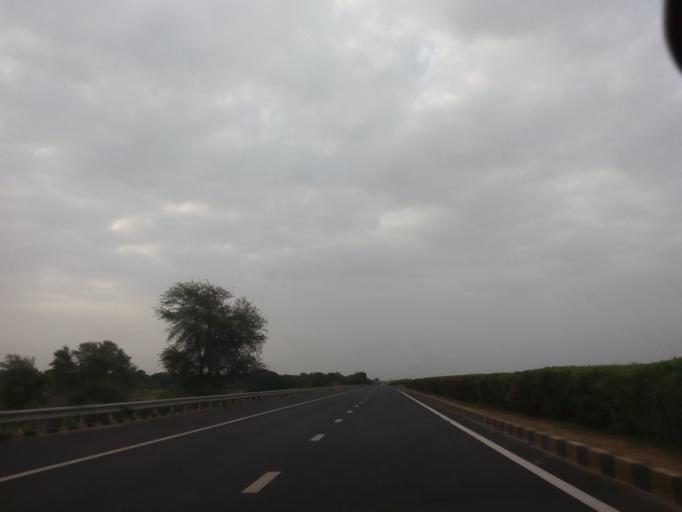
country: IN
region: Gujarat
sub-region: Ahmadabad
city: Naroda
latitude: 22.9594
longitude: 72.6795
